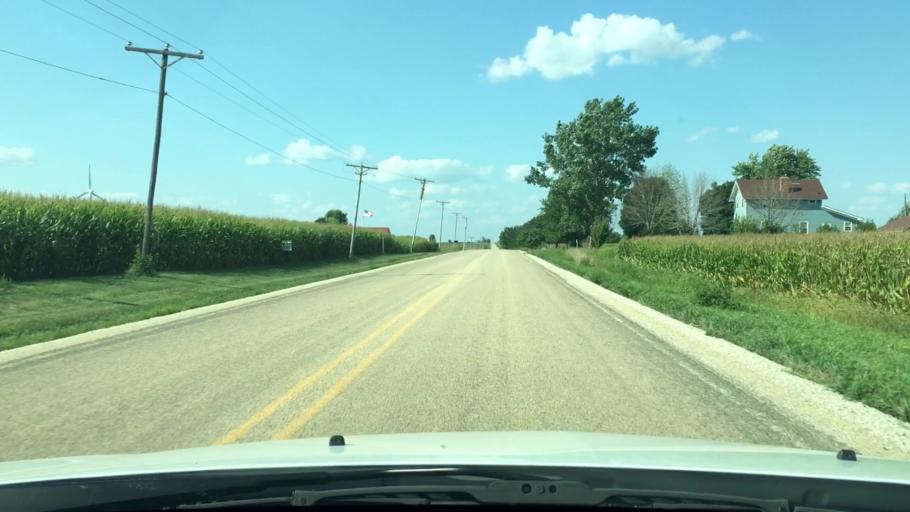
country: US
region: Illinois
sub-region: DeKalb County
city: Waterman
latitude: 41.8102
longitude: -88.7734
